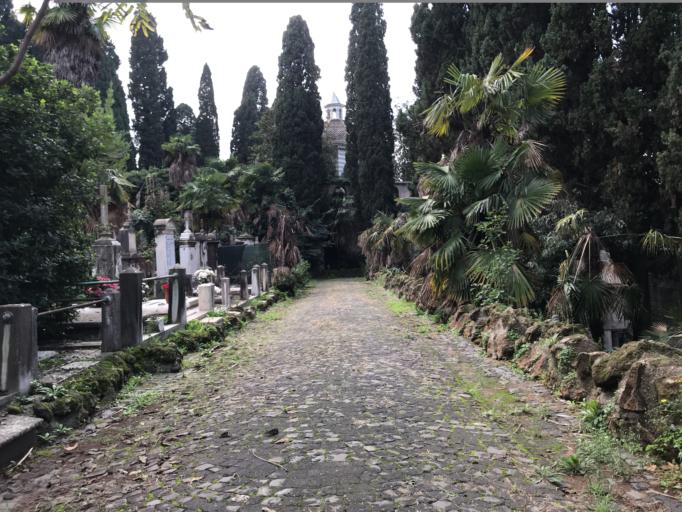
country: IT
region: Latium
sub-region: Citta metropolitana di Roma Capitale
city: Rome
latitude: 41.9039
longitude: 12.5213
